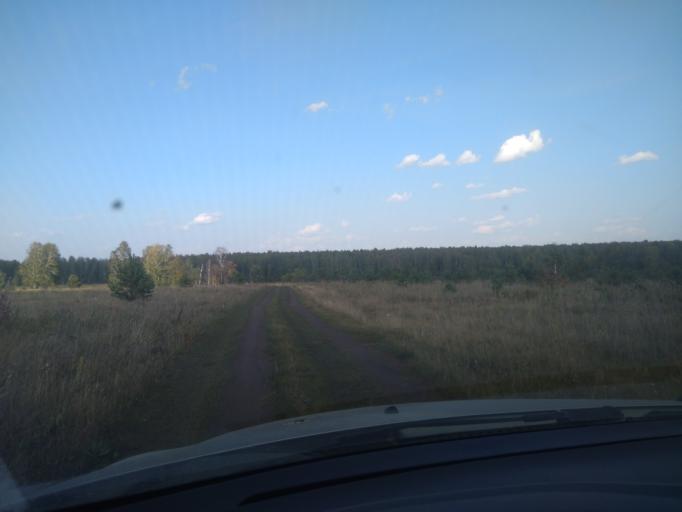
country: RU
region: Sverdlovsk
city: Pokrovskoye
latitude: 56.4248
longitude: 61.6094
